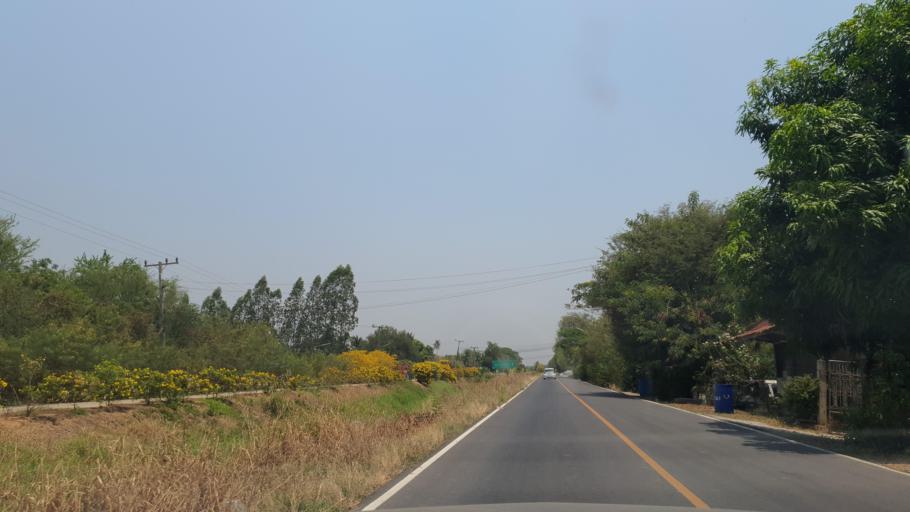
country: TH
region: Suphan Buri
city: Si Prachan
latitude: 14.6091
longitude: 100.1012
